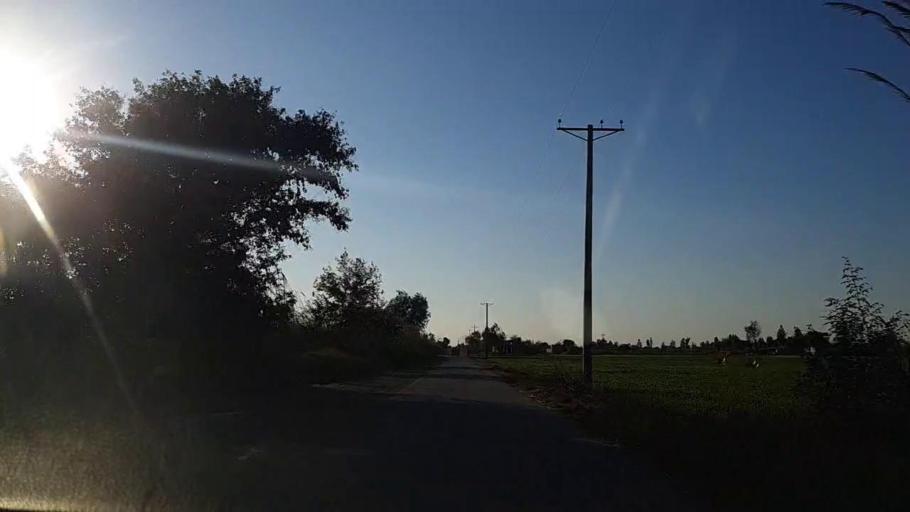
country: PK
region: Sindh
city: Khadro
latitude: 26.2790
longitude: 68.8903
